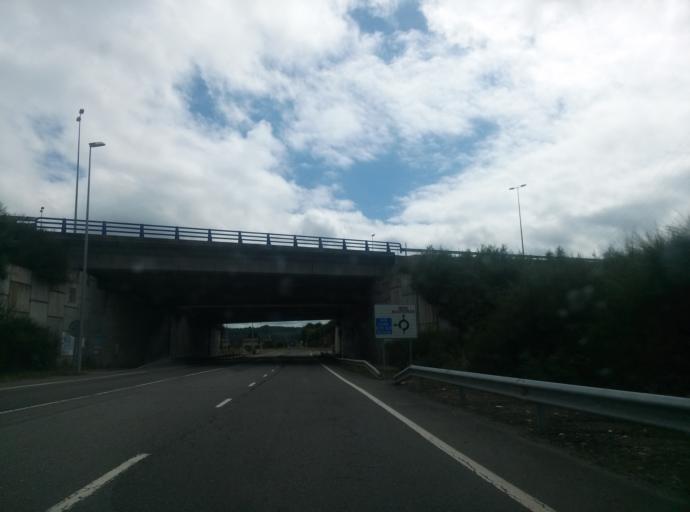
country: ES
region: Galicia
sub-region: Provincia de Lugo
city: Begonte
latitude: 43.1808
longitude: -7.7542
